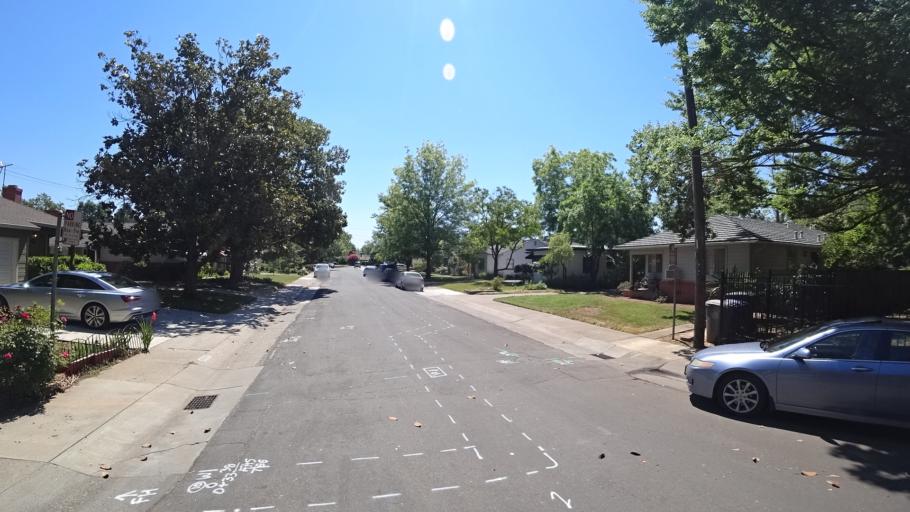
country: US
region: California
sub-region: Sacramento County
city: Sacramento
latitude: 38.5457
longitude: -121.4889
